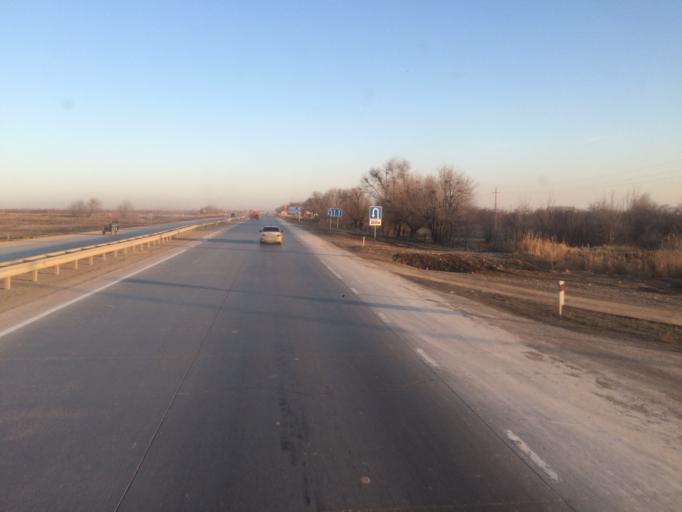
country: KZ
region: Ongtustik Qazaqstan
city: Turkestan
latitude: 43.2717
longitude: 68.3456
